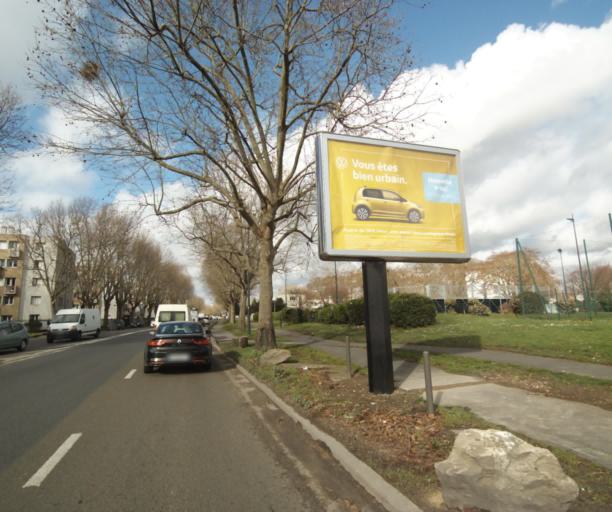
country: FR
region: Ile-de-France
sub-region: Departement de Seine-Saint-Denis
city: Saint-Denis
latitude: 48.9399
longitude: 2.3686
